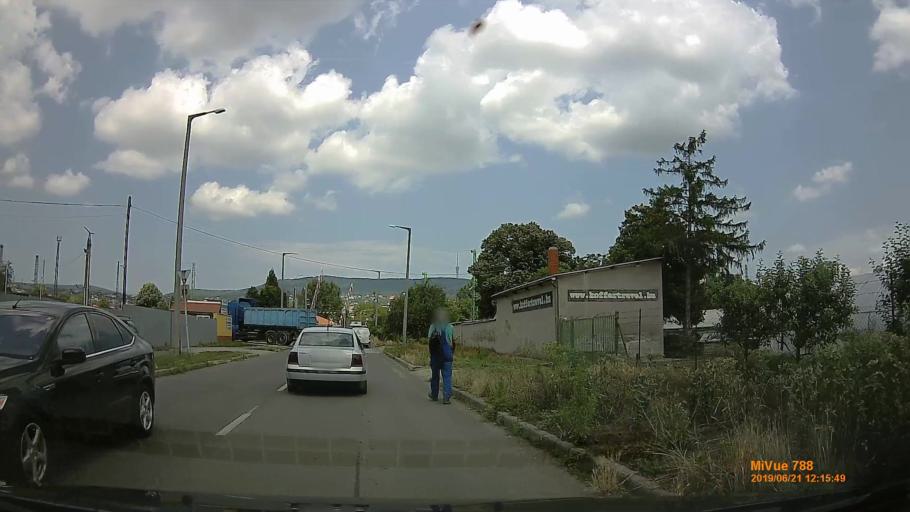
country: HU
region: Baranya
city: Pecs
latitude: 46.0630
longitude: 18.2134
